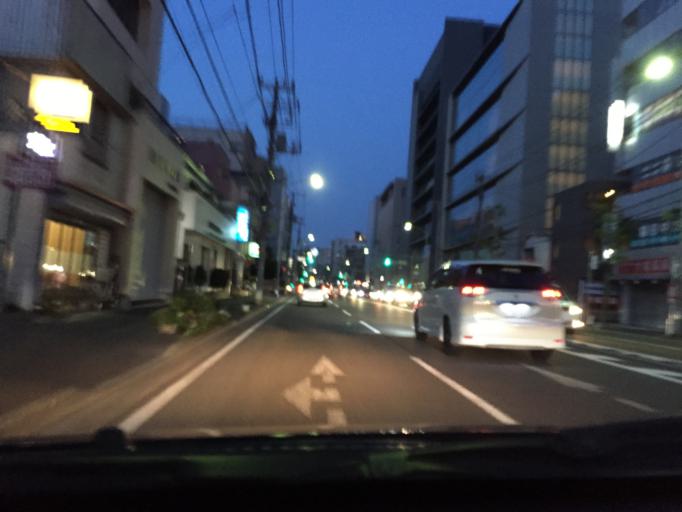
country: JP
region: Kanagawa
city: Yokohama
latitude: 35.4284
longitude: 139.6074
